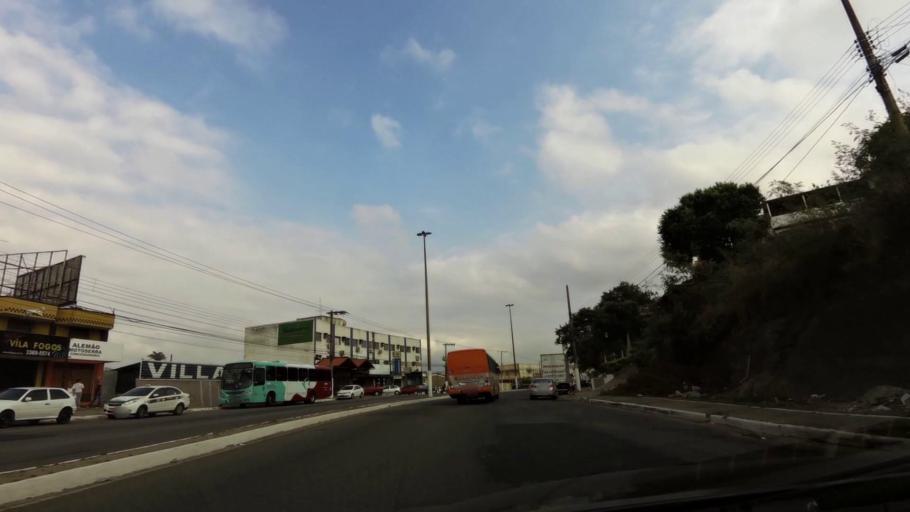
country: BR
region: Espirito Santo
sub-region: Vitoria
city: Vitoria
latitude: -20.3489
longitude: -40.3499
